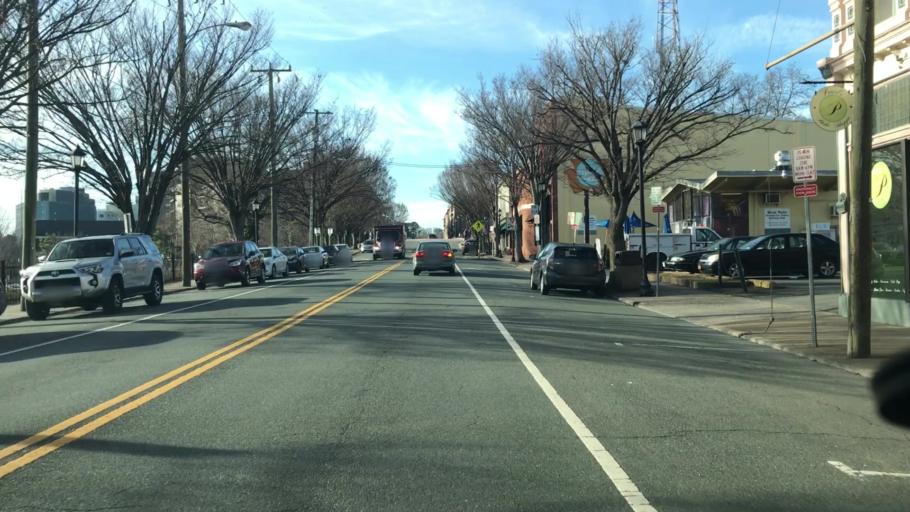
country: US
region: Virginia
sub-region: City of Charlottesville
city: Charlottesville
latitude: 38.0316
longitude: -78.4901
